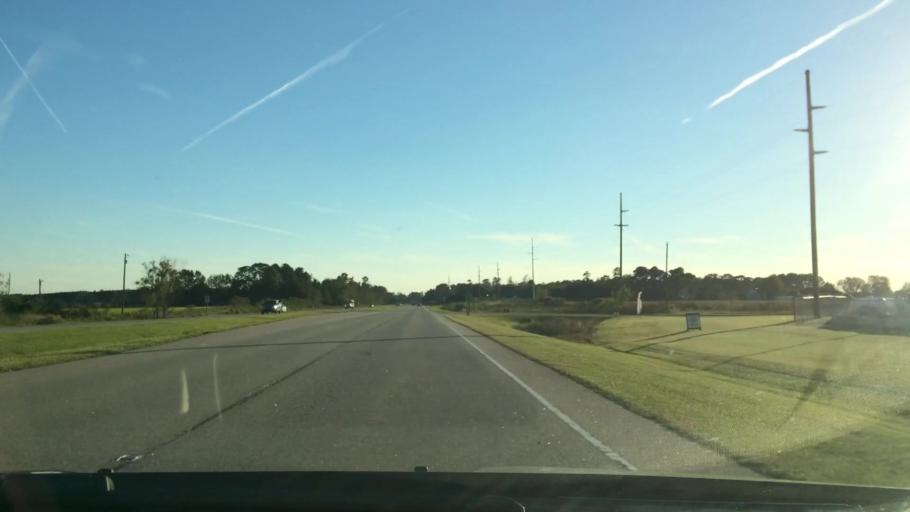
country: US
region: North Carolina
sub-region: Pitt County
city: Grifton
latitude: 35.3752
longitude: -77.4534
